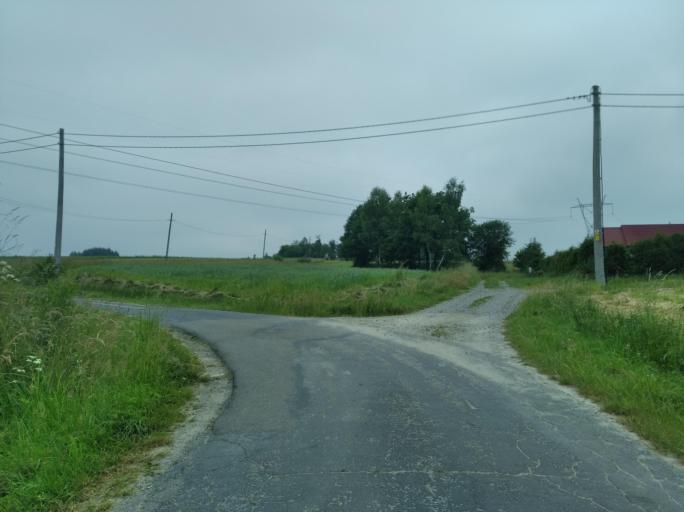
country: PL
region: Subcarpathian Voivodeship
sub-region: Powiat brzozowski
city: Jasienica Rosielna
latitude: 49.7573
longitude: 21.9229
